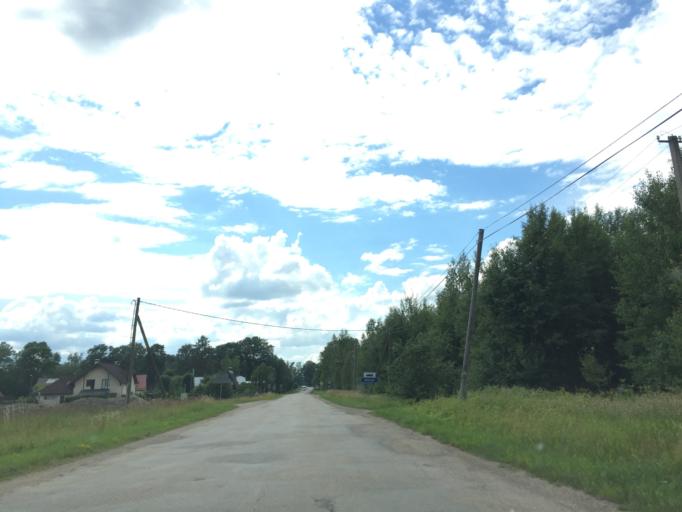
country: LV
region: Sigulda
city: Sigulda
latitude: 57.1595
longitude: 24.8914
